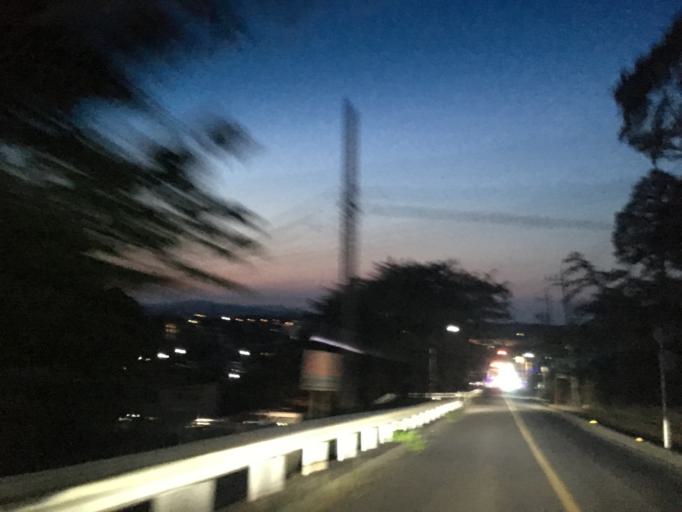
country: JP
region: Saitama
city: Sayama
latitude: 35.8397
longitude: 139.3776
